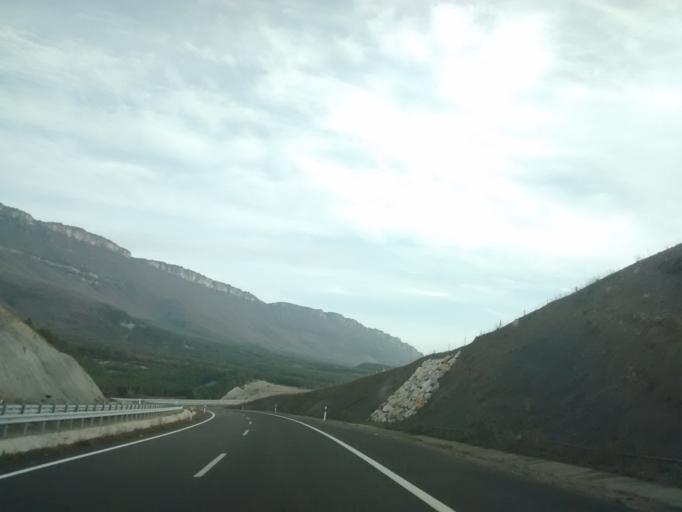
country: ES
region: Aragon
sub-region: Provincia de Zaragoza
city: Undues de Lerda
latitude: 42.6196
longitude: -1.1404
